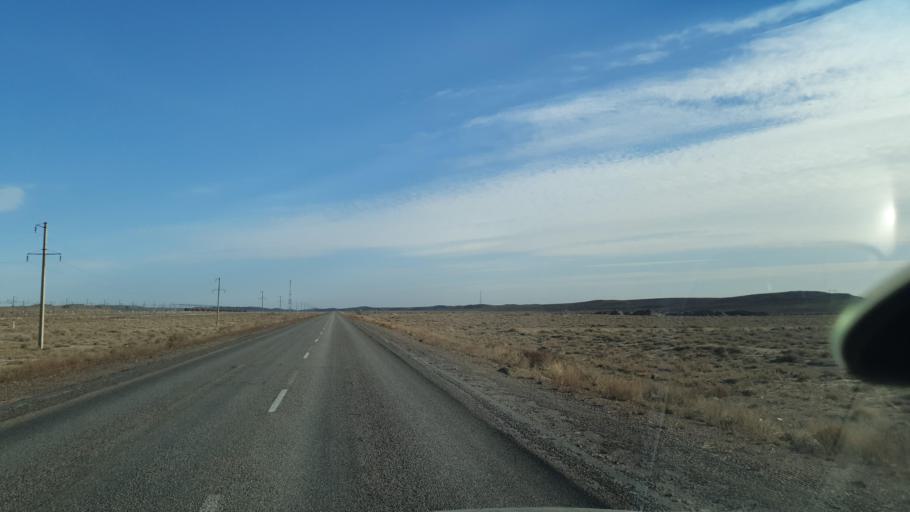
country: KZ
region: Zhambyl
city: Mynaral
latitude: 45.5598
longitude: 73.4362
